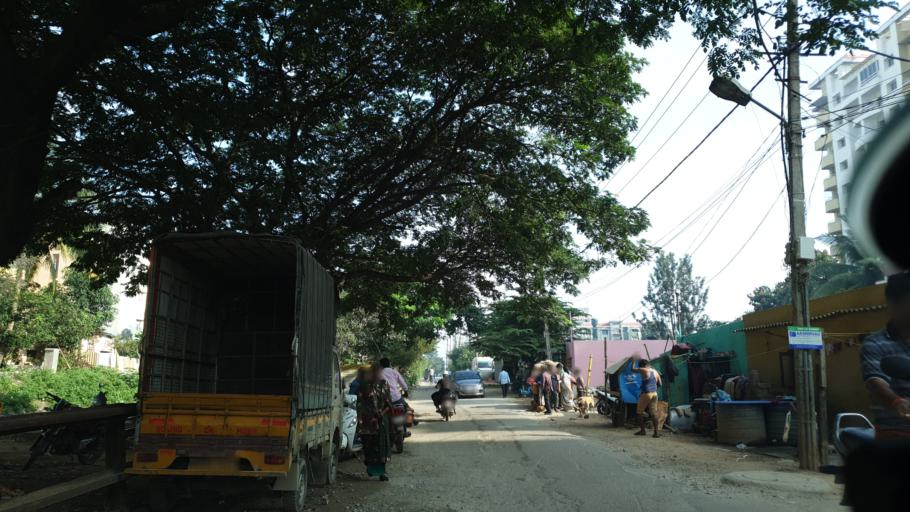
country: IN
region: Karnataka
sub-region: Bangalore Urban
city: Bangalore
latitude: 12.9588
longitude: 77.7045
